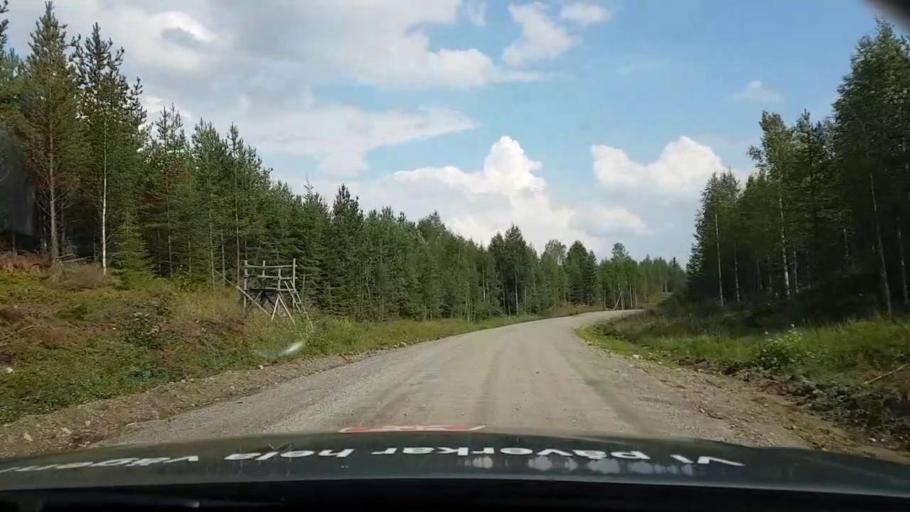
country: SE
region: Vaesternorrland
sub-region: Ange Kommun
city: Fransta
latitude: 62.7768
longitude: 15.9681
